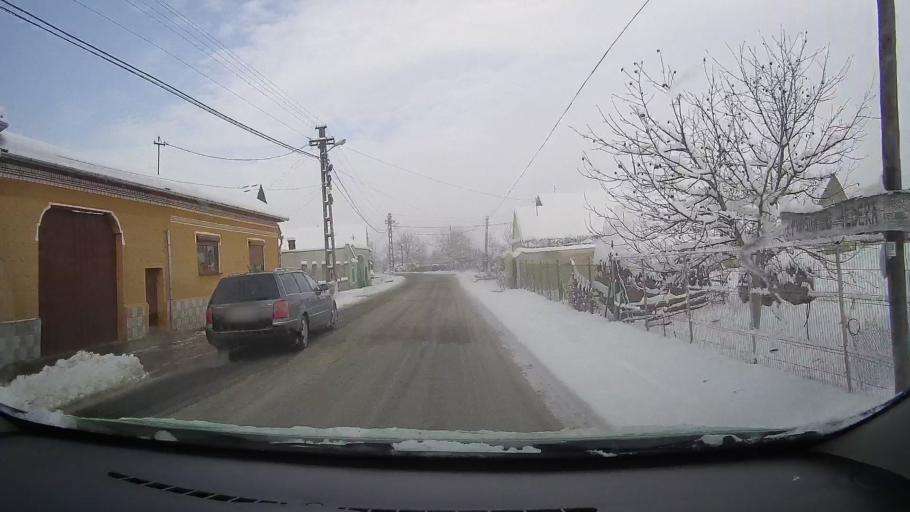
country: RO
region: Alba
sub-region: Comuna Pianu
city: Pianu de Jos
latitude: 45.9404
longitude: 23.4842
